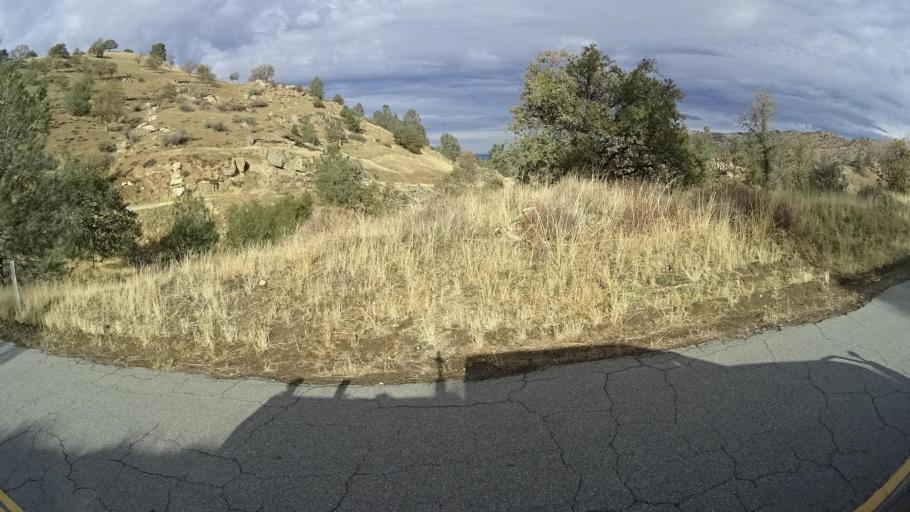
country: US
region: California
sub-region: Kern County
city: Golden Hills
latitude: 35.1900
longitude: -118.5231
